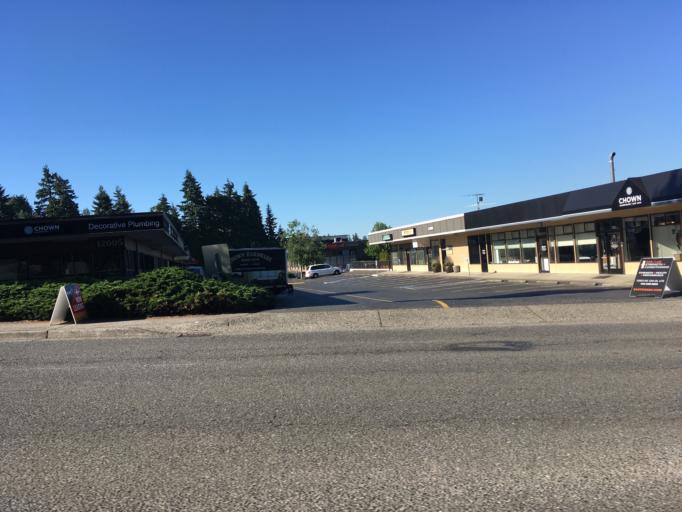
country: US
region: Washington
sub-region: King County
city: Bellevue
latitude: 47.6204
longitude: -122.1783
